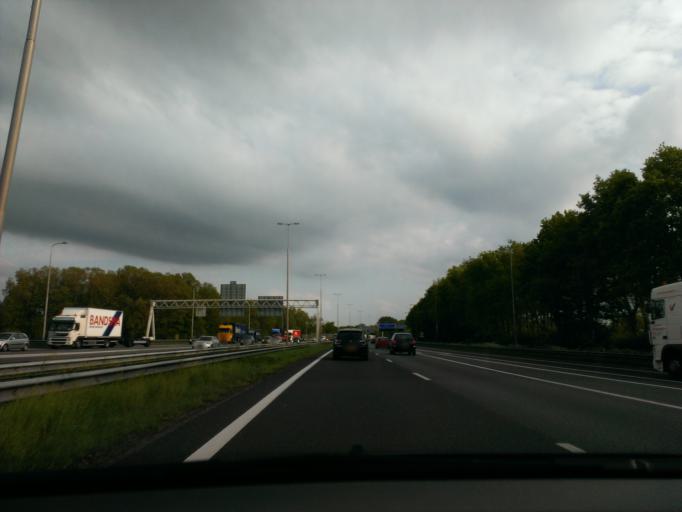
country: NL
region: Gelderland
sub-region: Gemeente Apeldoorn
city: Loenen
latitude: 52.1807
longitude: 6.0267
